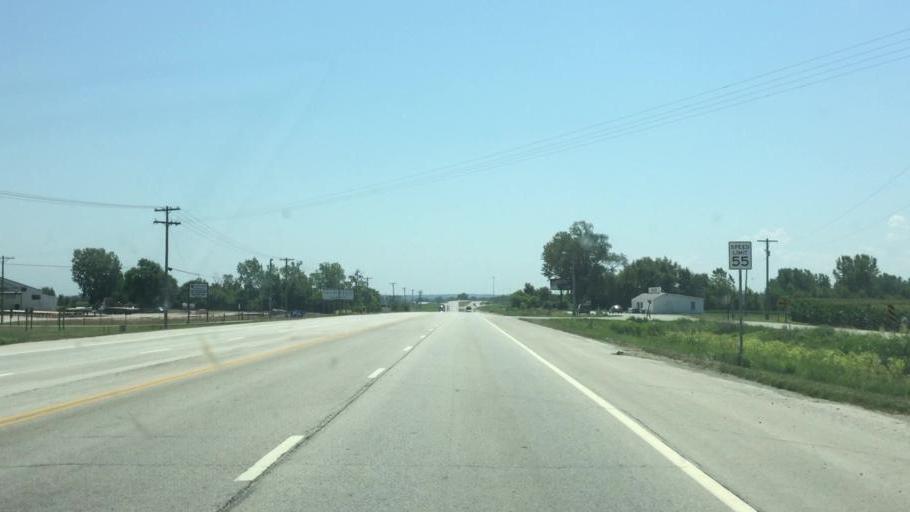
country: US
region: Kansas
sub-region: Doniphan County
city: Wathena
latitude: 39.7547
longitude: -94.9369
